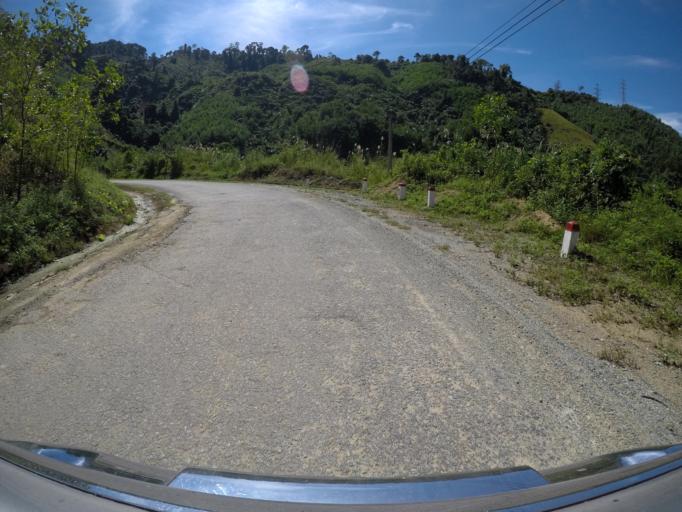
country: VN
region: Quang Nam
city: Thanh My
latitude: 15.6631
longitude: 107.6339
